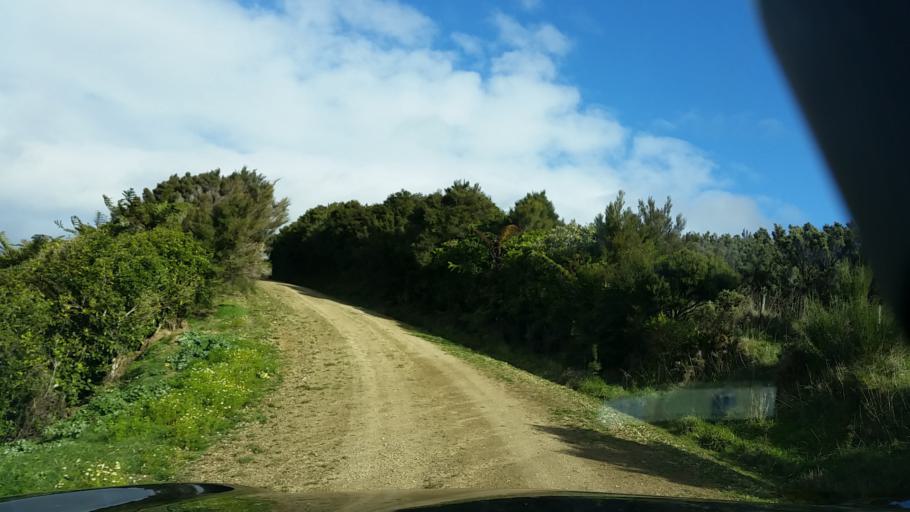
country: NZ
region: Marlborough
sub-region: Marlborough District
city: Picton
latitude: -40.9639
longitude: 173.9014
